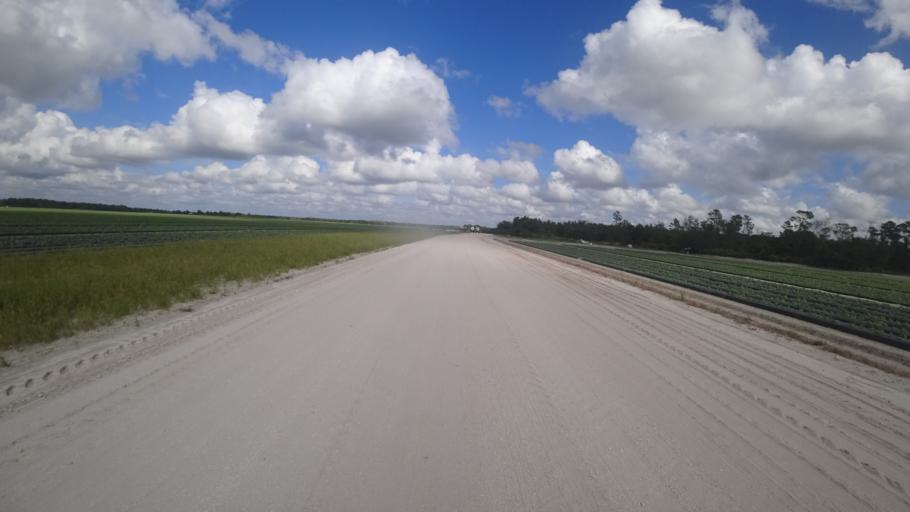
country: US
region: Florida
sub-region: Sarasota County
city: Lake Sarasota
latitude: 27.4146
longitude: -82.1889
